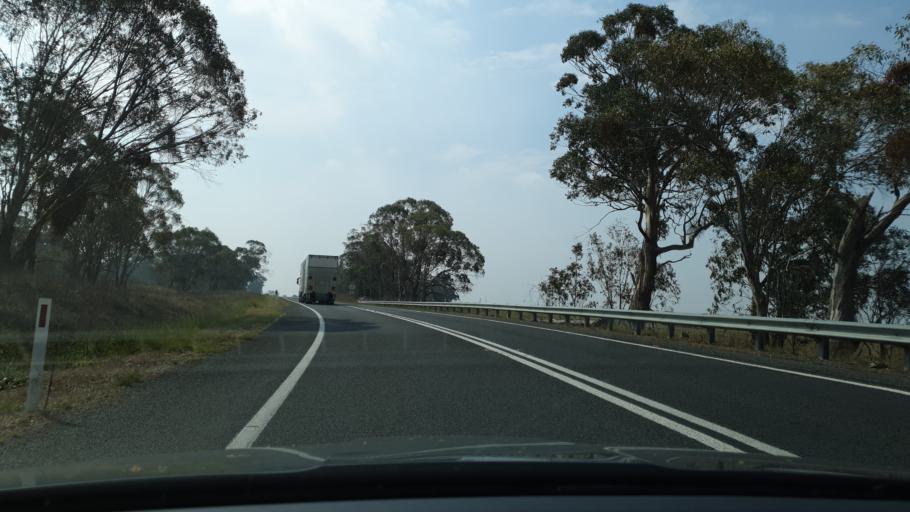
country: AU
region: New South Wales
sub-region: Guyra
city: Guyra
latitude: -30.0987
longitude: 151.7284
